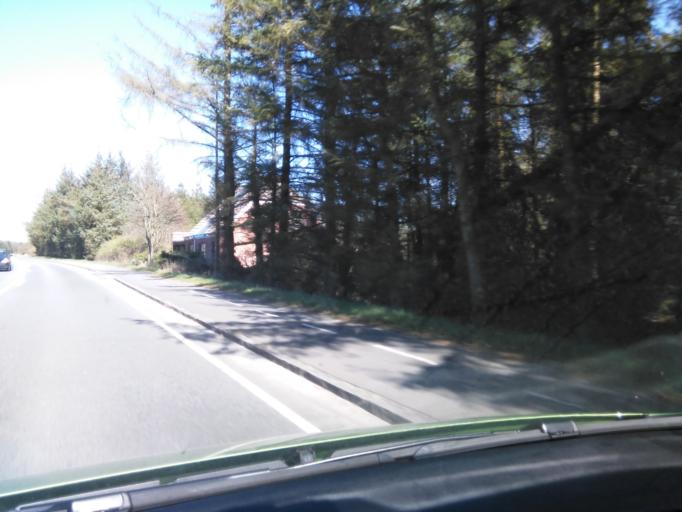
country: DK
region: South Denmark
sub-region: Varde Kommune
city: Oksbol
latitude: 55.5729
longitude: 8.2118
